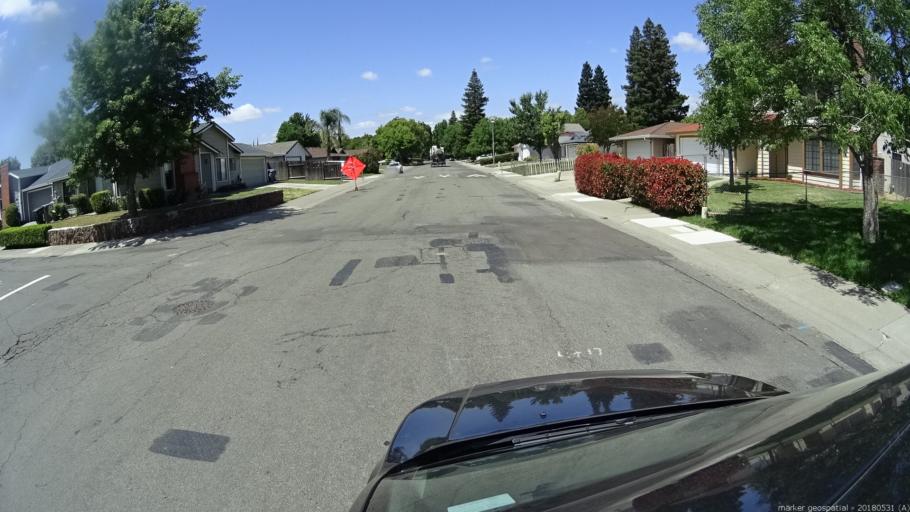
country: US
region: California
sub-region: Sacramento County
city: Sacramento
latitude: 38.6208
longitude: -121.5112
